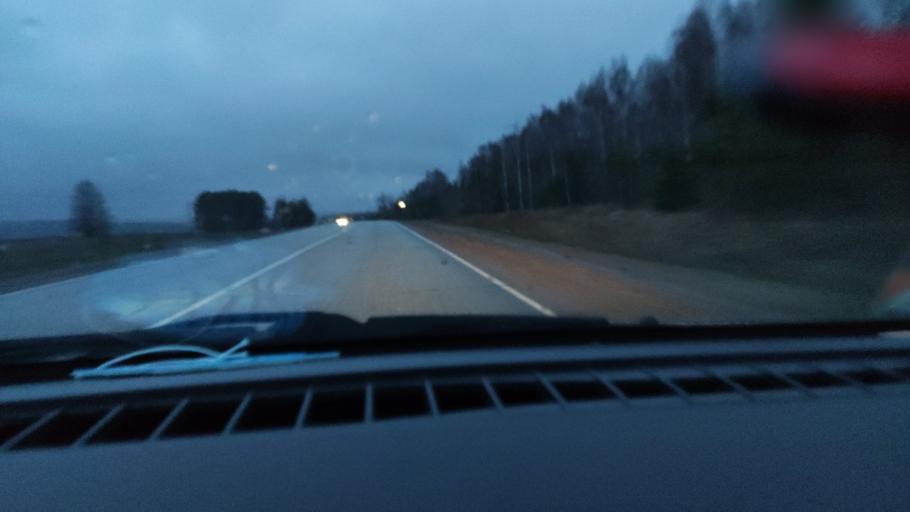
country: RU
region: Udmurtiya
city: Mozhga
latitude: 56.3440
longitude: 52.2842
